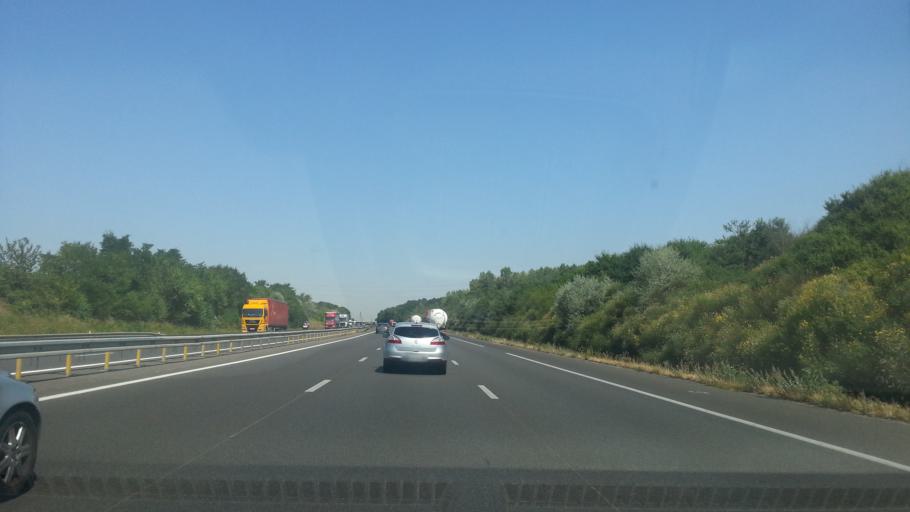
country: FR
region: Centre
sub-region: Departement du Loiret
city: Ingre
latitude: 47.9300
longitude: 1.8496
